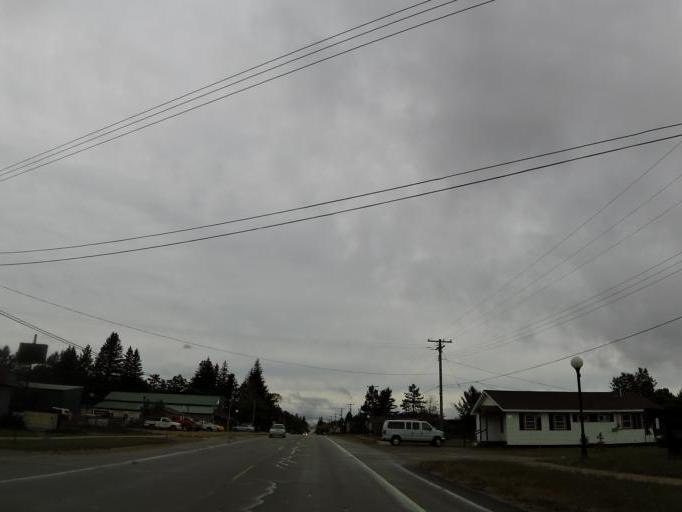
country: US
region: Michigan
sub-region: Roscommon County
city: Roscommon
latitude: 44.4933
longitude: -84.5835
